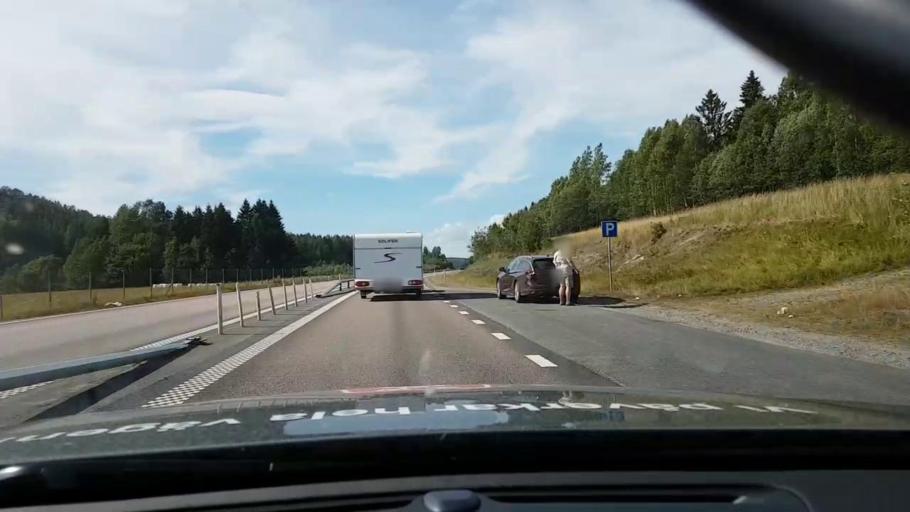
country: SE
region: Vaesternorrland
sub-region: OErnskoeldsviks Kommun
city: Ornskoldsvik
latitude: 63.3114
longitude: 18.8276
